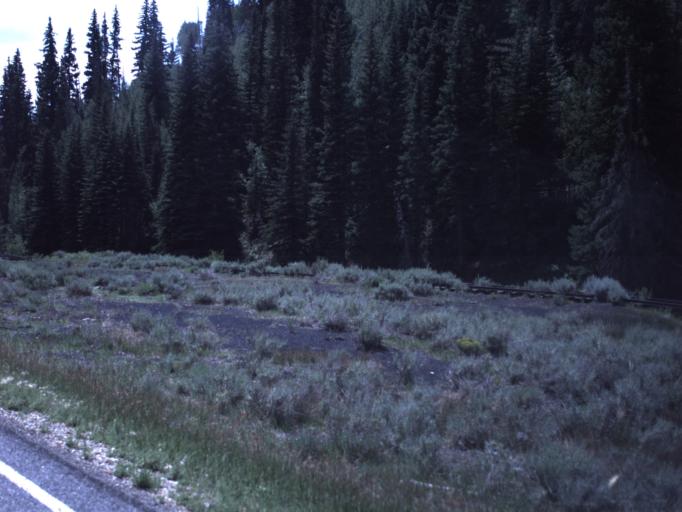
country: US
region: Utah
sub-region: Sanpete County
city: Fairview
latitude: 39.6547
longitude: -111.1539
